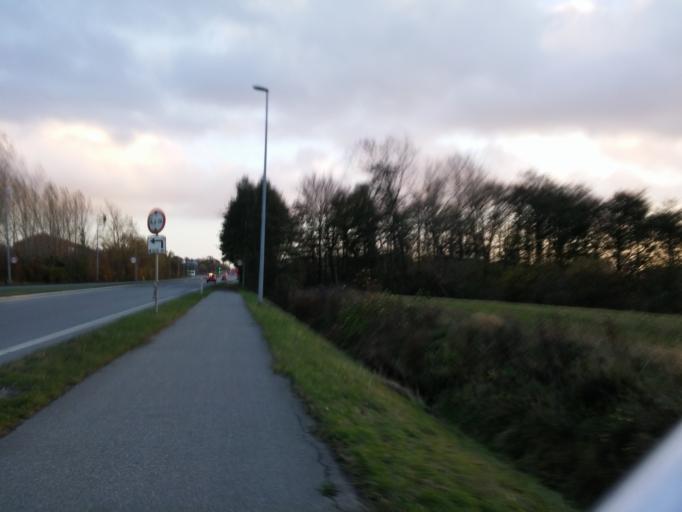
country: DK
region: South Denmark
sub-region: Kerteminde Kommune
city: Munkebo
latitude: 55.4553
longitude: 10.5374
